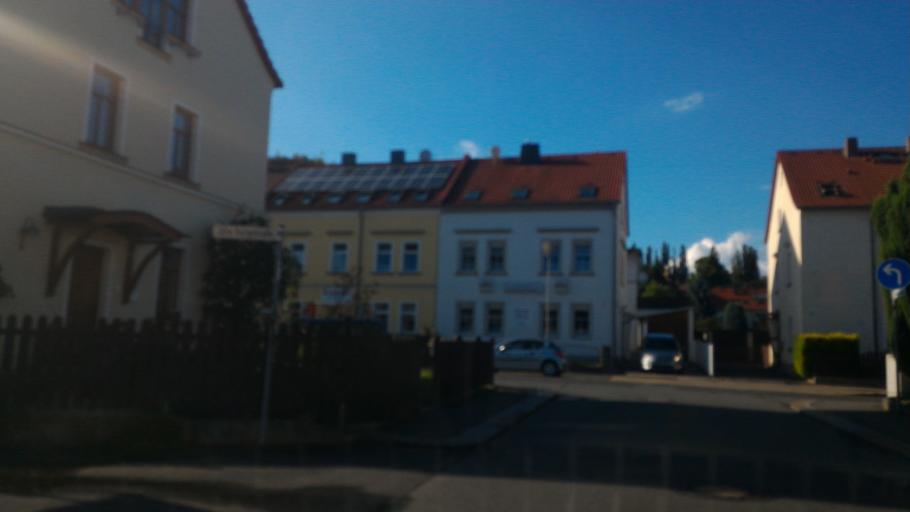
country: DE
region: Saxony
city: Zittau
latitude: 50.8974
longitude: 14.7898
